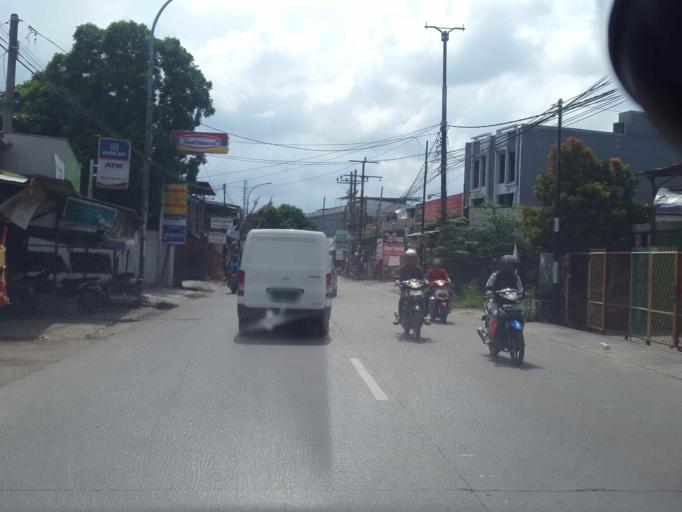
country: ID
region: West Java
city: Bekasi
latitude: -6.2733
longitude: 106.9786
